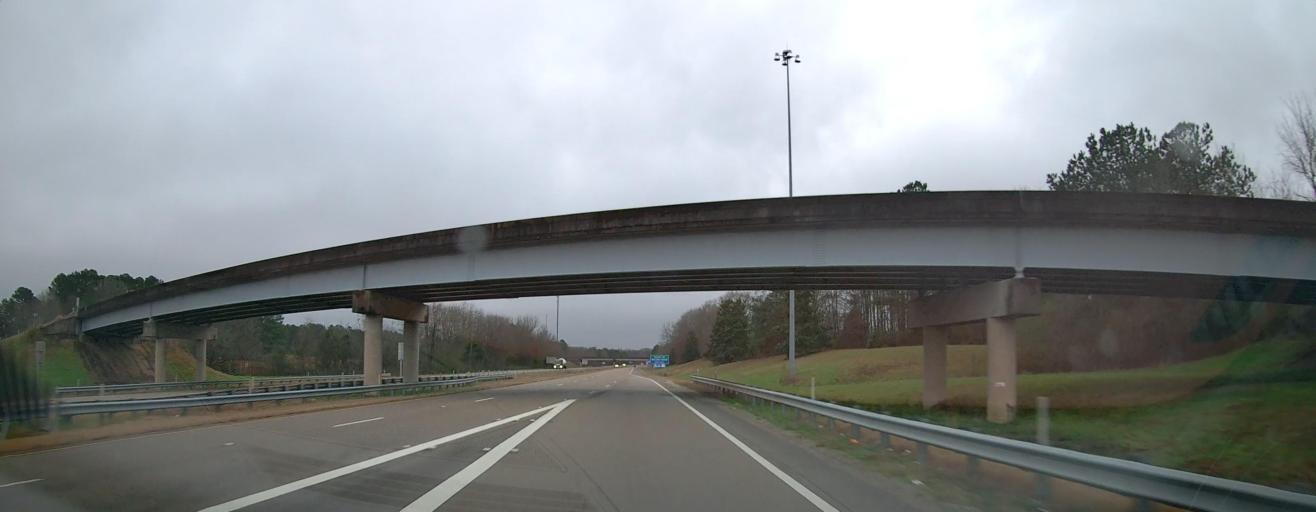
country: US
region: Mississippi
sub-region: Alcorn County
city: Corinth
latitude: 34.9283
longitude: -88.5471
